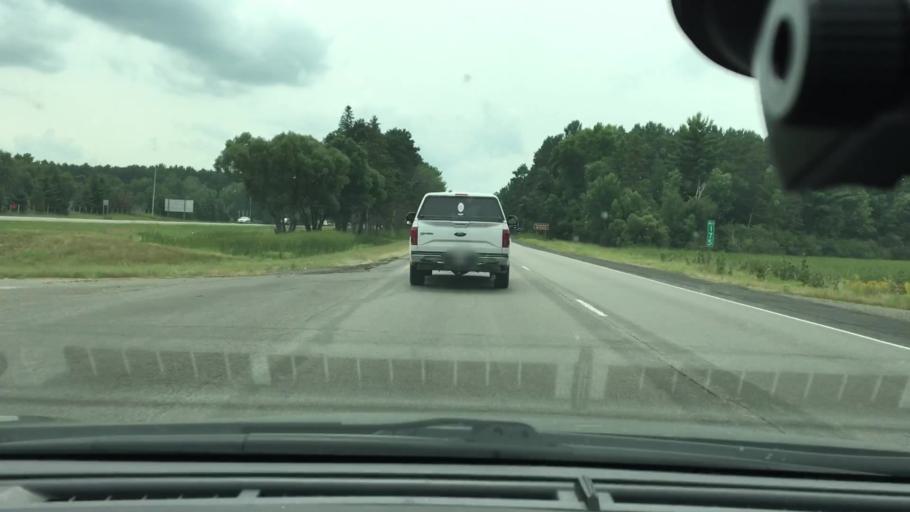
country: US
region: Minnesota
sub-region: Mille Lacs County
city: Princeton
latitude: 45.5272
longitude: -93.5832
